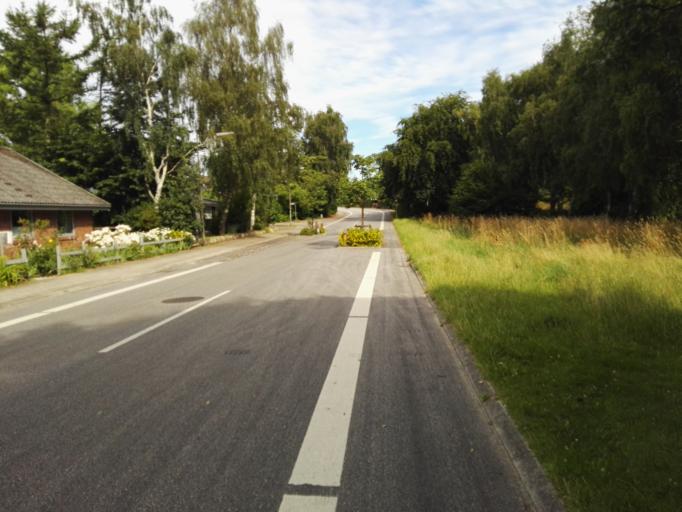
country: DK
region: Capital Region
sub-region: Halsnaes Kommune
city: Hundested
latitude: 55.9697
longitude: 11.8660
